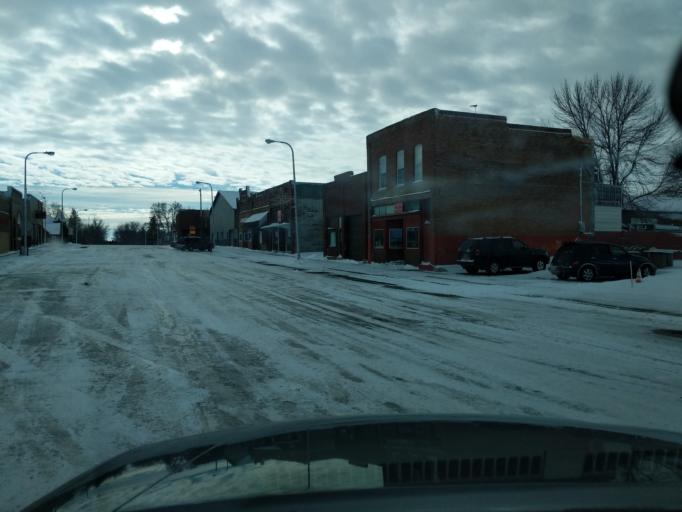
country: US
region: Minnesota
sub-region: Renville County
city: Renville
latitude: 44.7879
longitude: -95.3515
